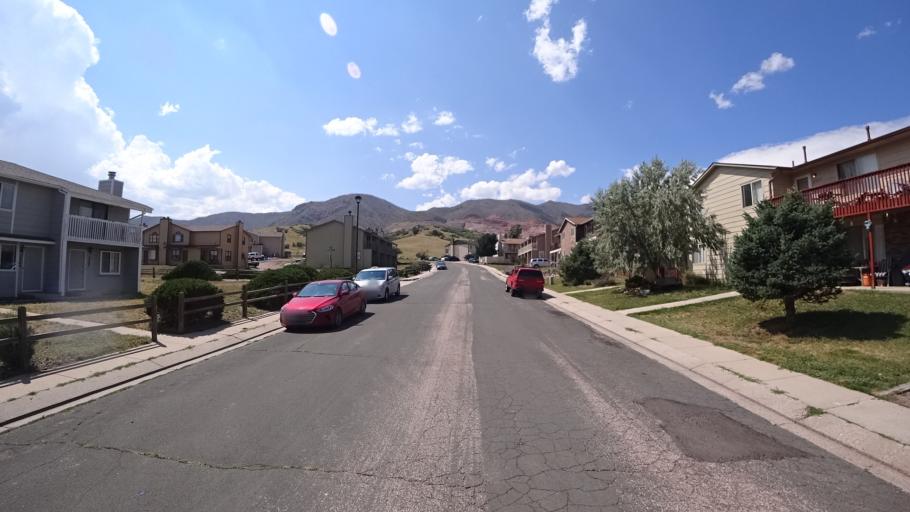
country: US
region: Colorado
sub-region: El Paso County
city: Air Force Academy
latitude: 38.9327
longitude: -104.8722
